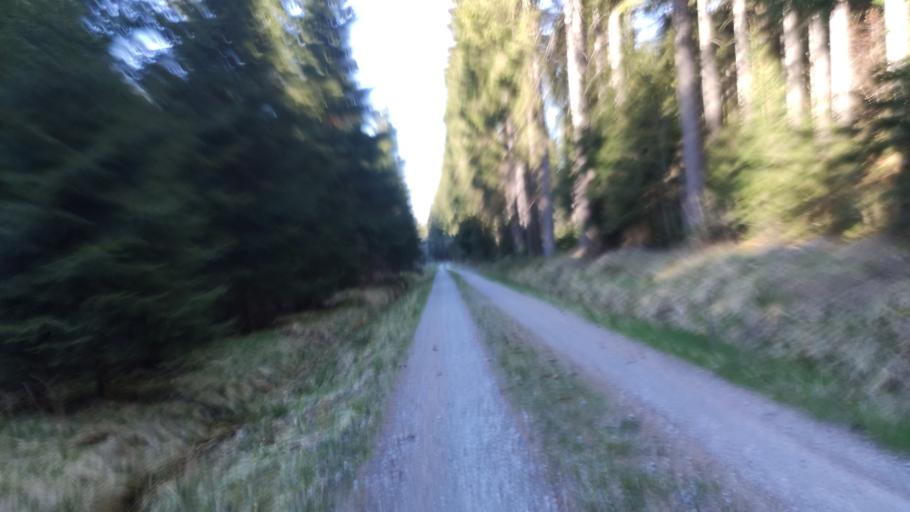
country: DE
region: Bavaria
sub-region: Upper Franconia
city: Reichenbach
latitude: 50.4442
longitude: 11.4378
